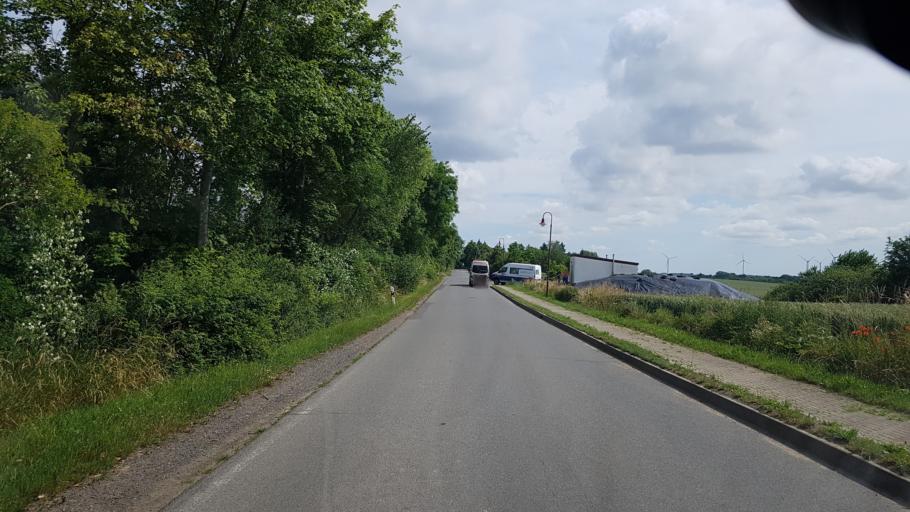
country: DE
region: Mecklenburg-Vorpommern
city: Strasburg
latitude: 53.4268
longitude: 13.6965
